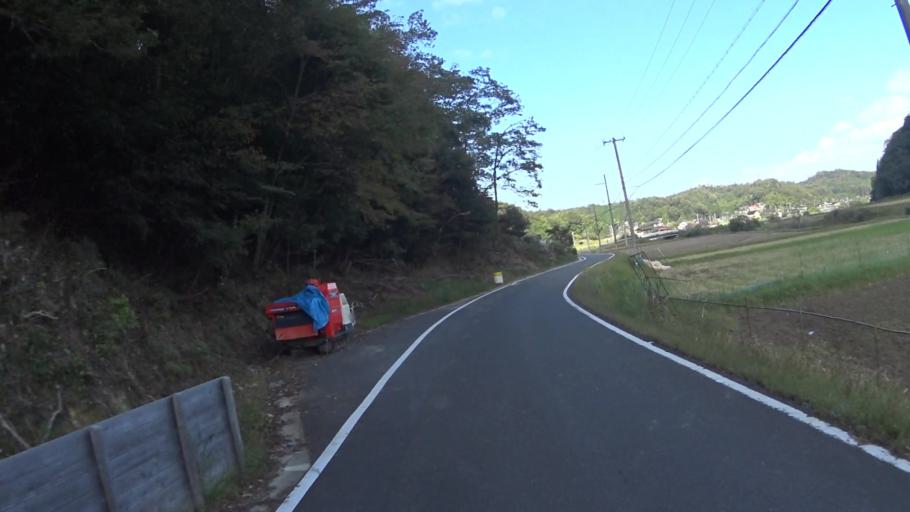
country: JP
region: Kyoto
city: Miyazu
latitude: 35.5747
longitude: 135.0167
